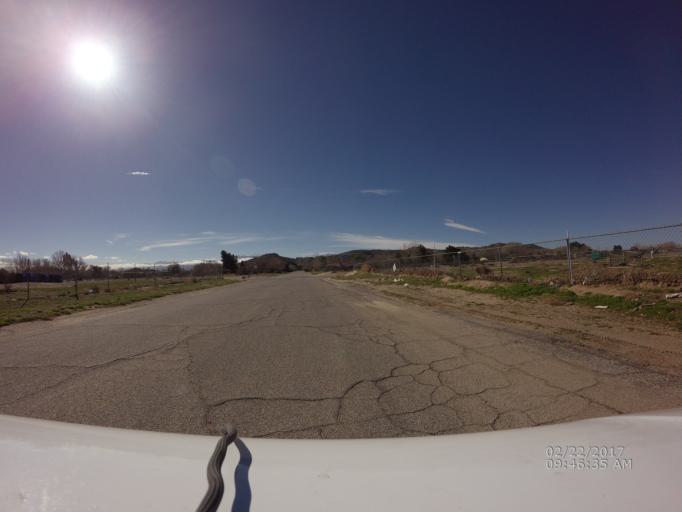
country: US
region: California
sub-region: Los Angeles County
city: Lake Los Angeles
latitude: 34.6245
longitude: -117.8404
